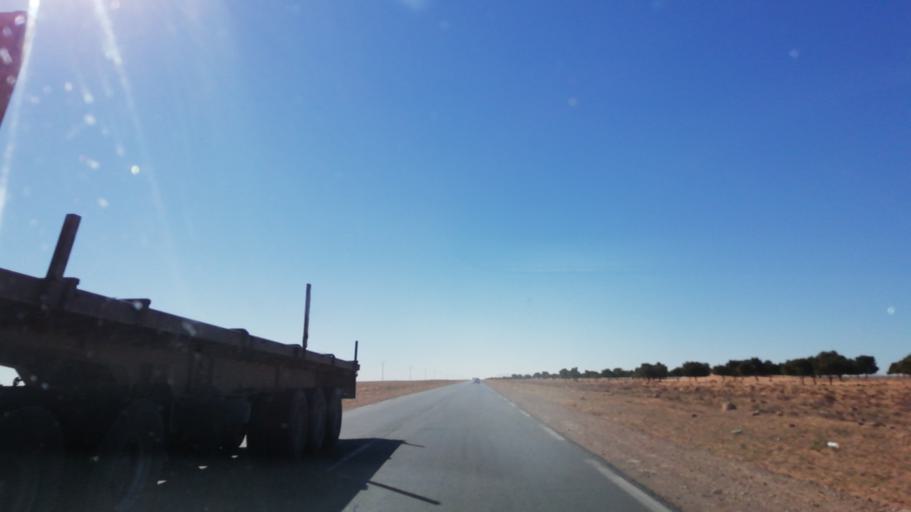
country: DZ
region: Saida
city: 'Ain el Hadjar
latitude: 33.9963
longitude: 0.0399
